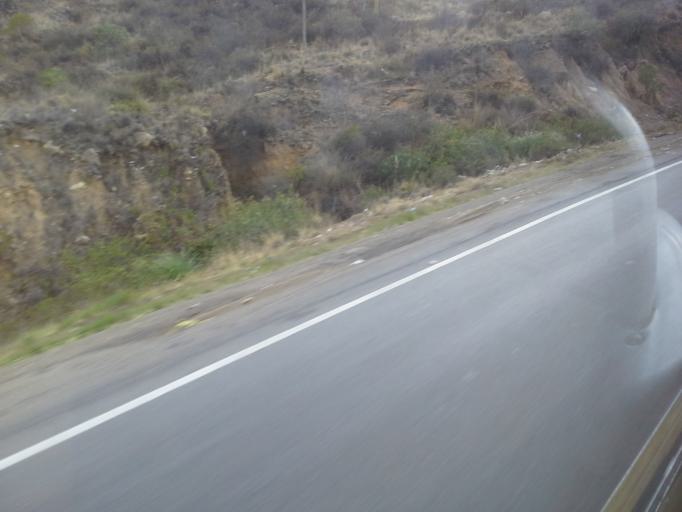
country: BO
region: Cochabamba
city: Colomi
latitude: -17.4108
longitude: -65.9655
